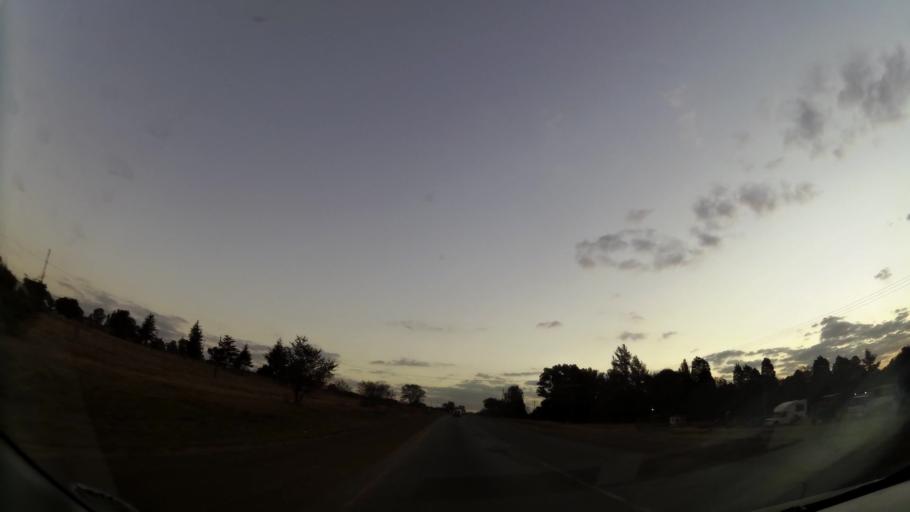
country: ZA
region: Gauteng
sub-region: West Rand District Municipality
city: Krugersdorp
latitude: -26.0674
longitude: 27.6889
